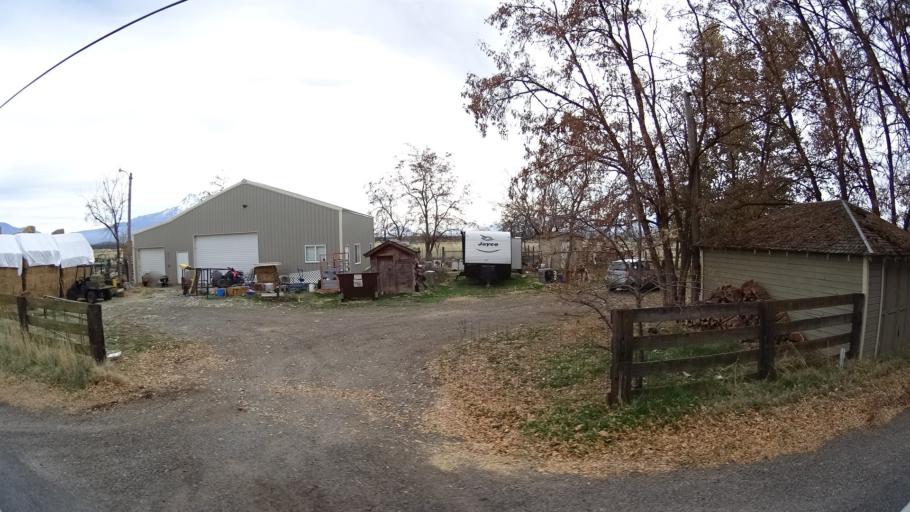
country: US
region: California
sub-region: Siskiyou County
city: Montague
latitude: 41.6239
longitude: -122.3892
